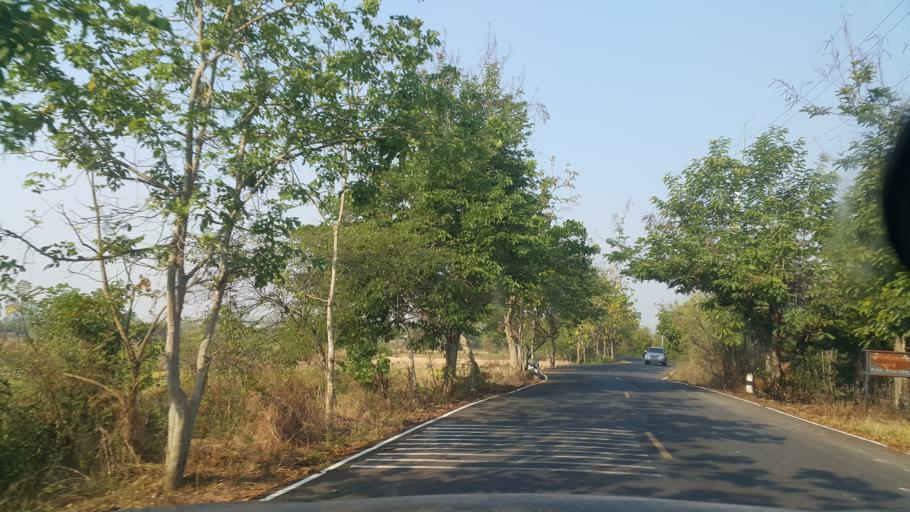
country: TH
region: Lamphun
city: Ban Thi
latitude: 18.6501
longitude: 99.0867
